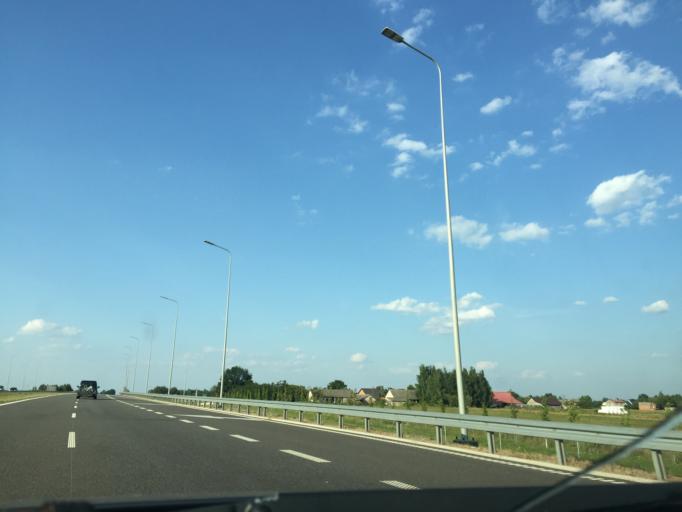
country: PL
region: Masovian Voivodeship
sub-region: Powiat radomski
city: Zakrzew
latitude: 51.4483
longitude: 21.0362
